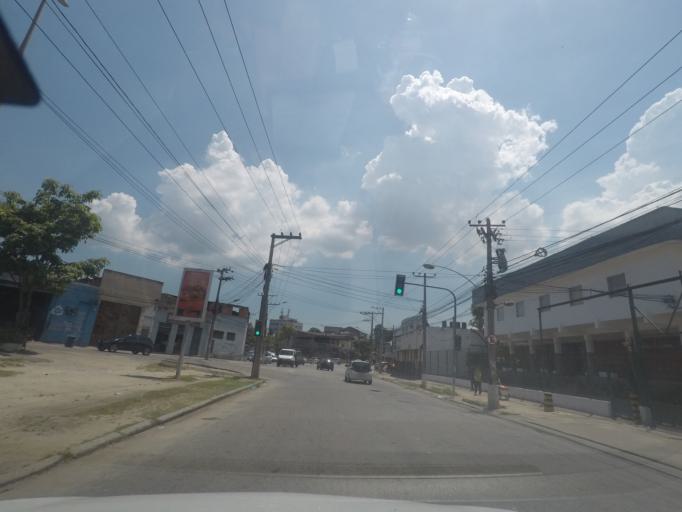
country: BR
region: Rio de Janeiro
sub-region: Rio De Janeiro
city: Rio de Janeiro
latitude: -22.8674
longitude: -43.2574
